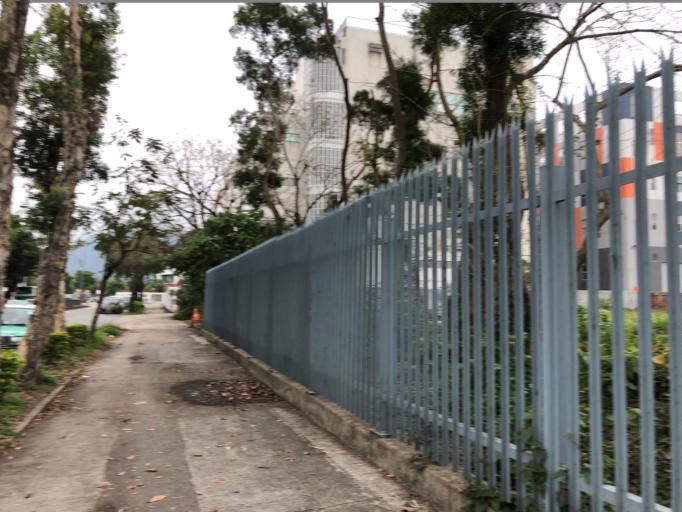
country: HK
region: Tai Po
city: Tai Po
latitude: 22.4552
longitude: 114.1882
